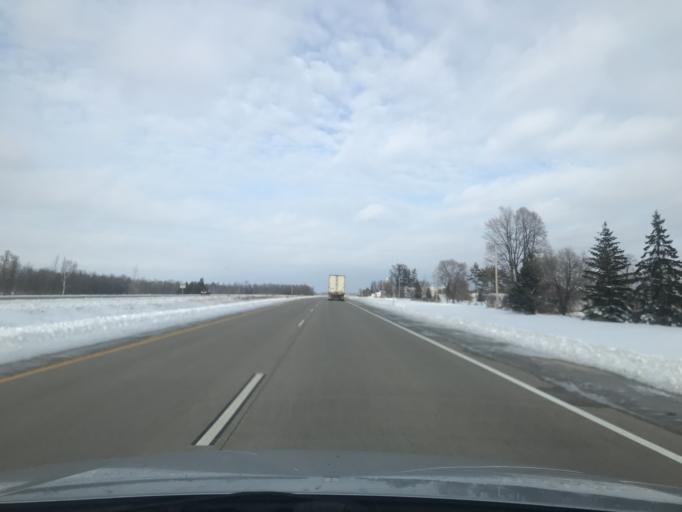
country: US
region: Wisconsin
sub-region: Marinette County
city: Peshtigo
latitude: 45.0046
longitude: -87.8488
